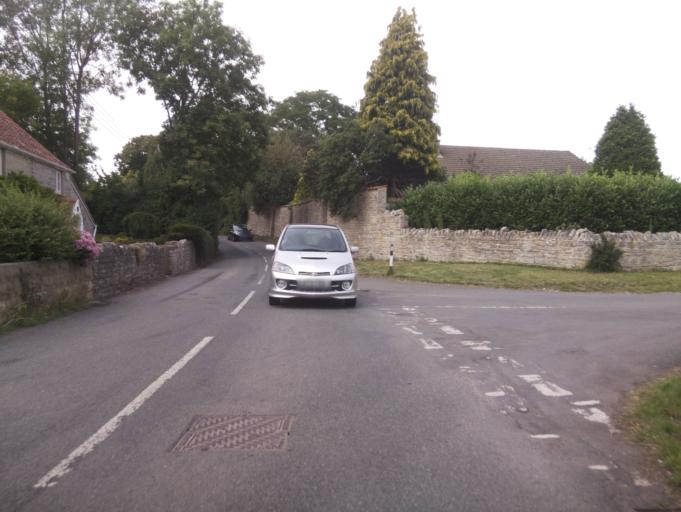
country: GB
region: England
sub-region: Somerset
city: Glastonbury
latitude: 51.0998
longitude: -2.6872
